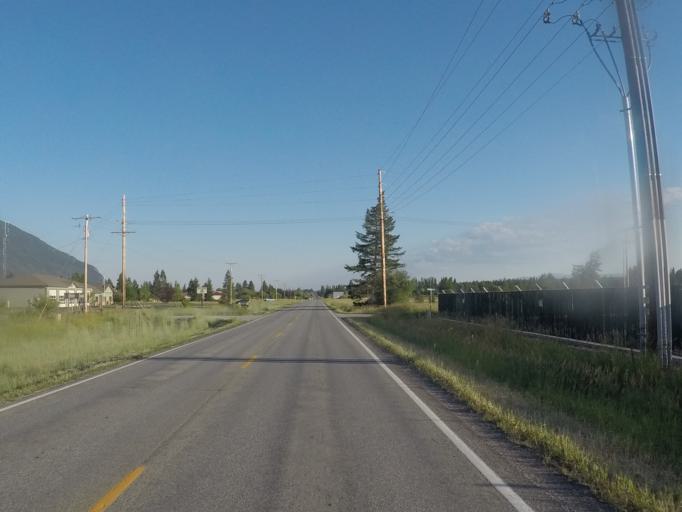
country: US
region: Montana
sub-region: Flathead County
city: Columbia Falls
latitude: 48.3508
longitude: -114.1593
